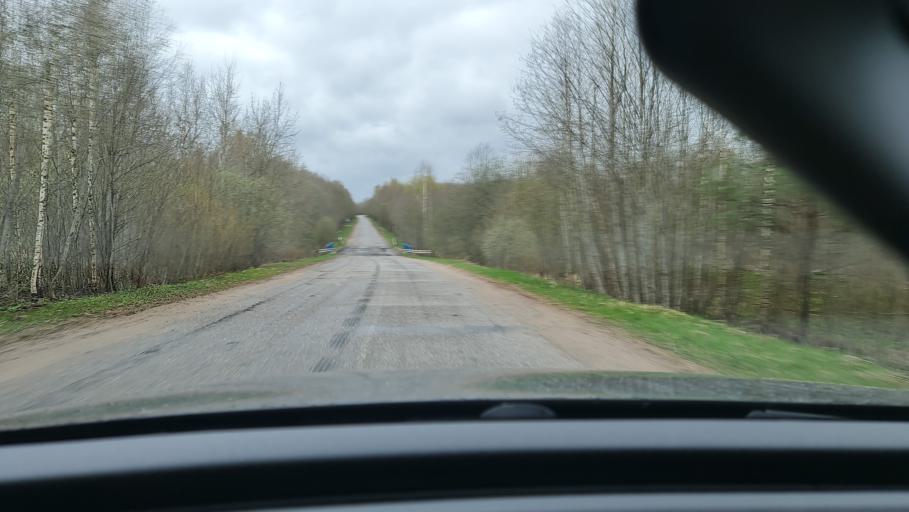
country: RU
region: Novgorod
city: Marevo
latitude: 57.1044
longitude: 31.7633
